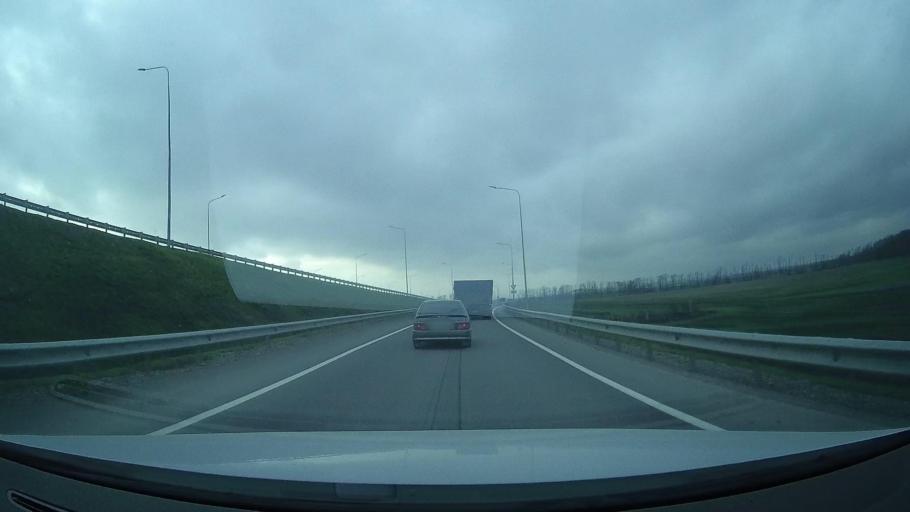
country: RU
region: Rostov
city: Grushevskaya
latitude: 47.5025
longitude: 39.9685
